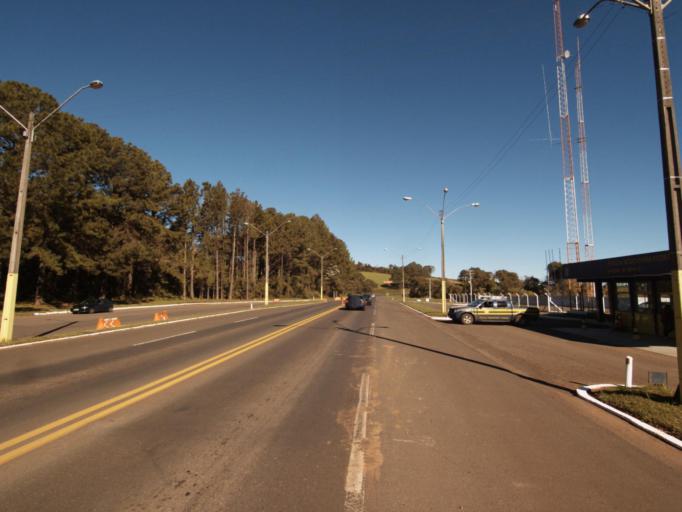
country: BR
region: Santa Catarina
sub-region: Xanxere
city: Xanxere
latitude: -26.9014
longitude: -52.4631
